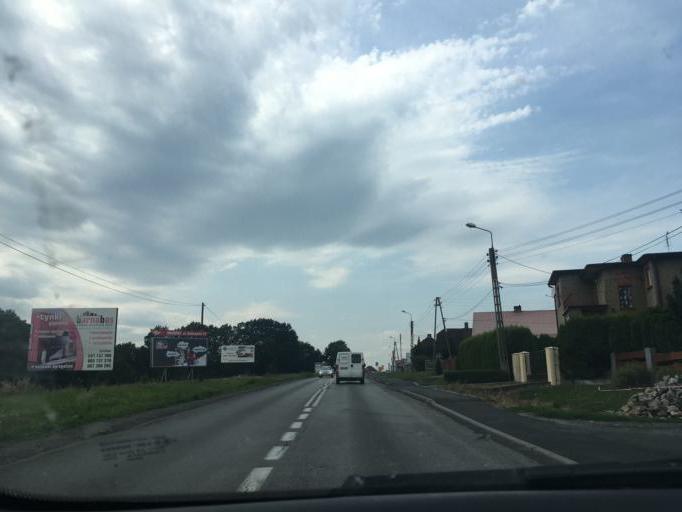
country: PL
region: Silesian Voivodeship
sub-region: Powiat raciborski
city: Kornowac
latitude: 50.0739
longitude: 18.3143
